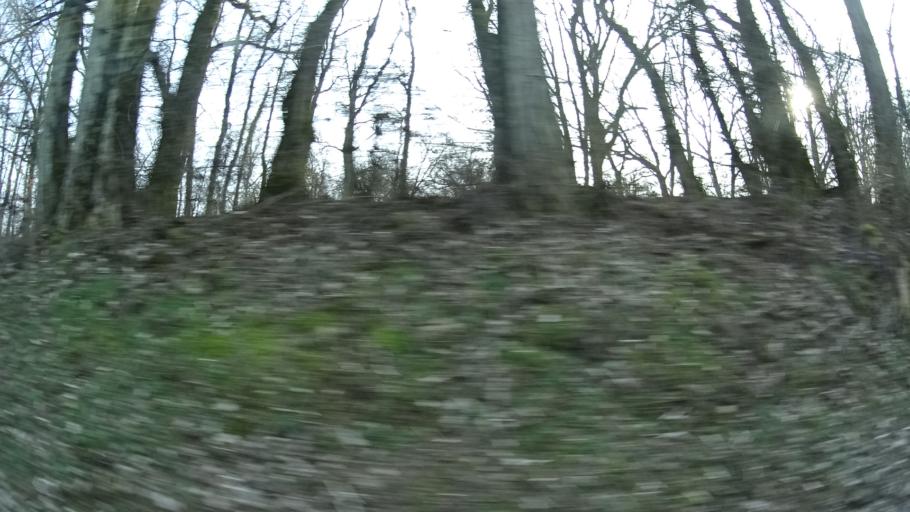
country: DE
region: Rheinland-Pfalz
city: Oberstaufenbach
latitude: 49.5064
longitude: 7.5215
